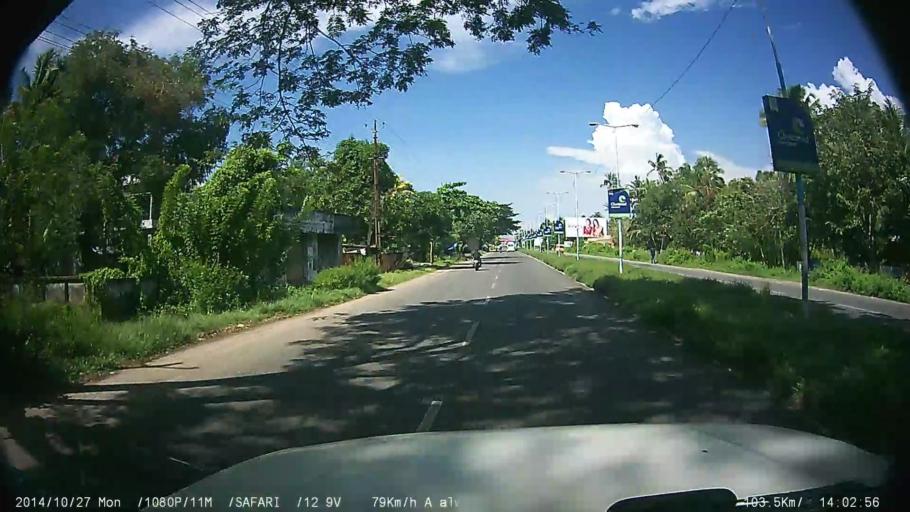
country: IN
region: Kerala
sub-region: Alappuzha
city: Vayalar
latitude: 9.7153
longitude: 76.3174
